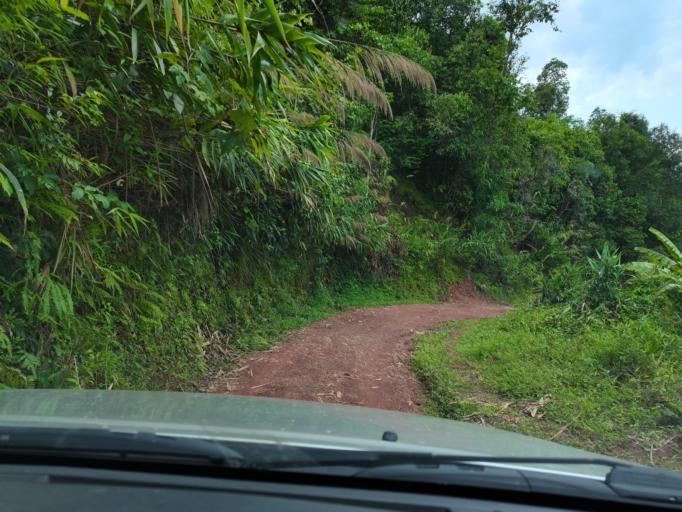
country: LA
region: Loungnamtha
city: Muang Nale
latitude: 20.5110
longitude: 101.0811
